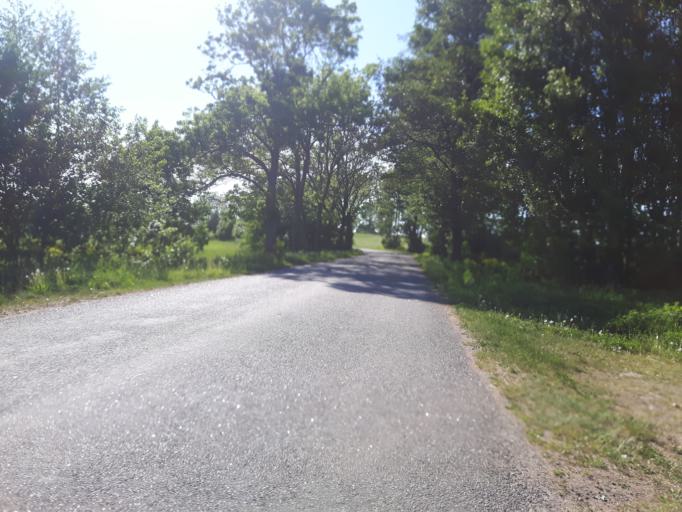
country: EE
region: Laeaene-Virumaa
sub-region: Haljala vald
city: Haljala
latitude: 59.5398
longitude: 26.0738
